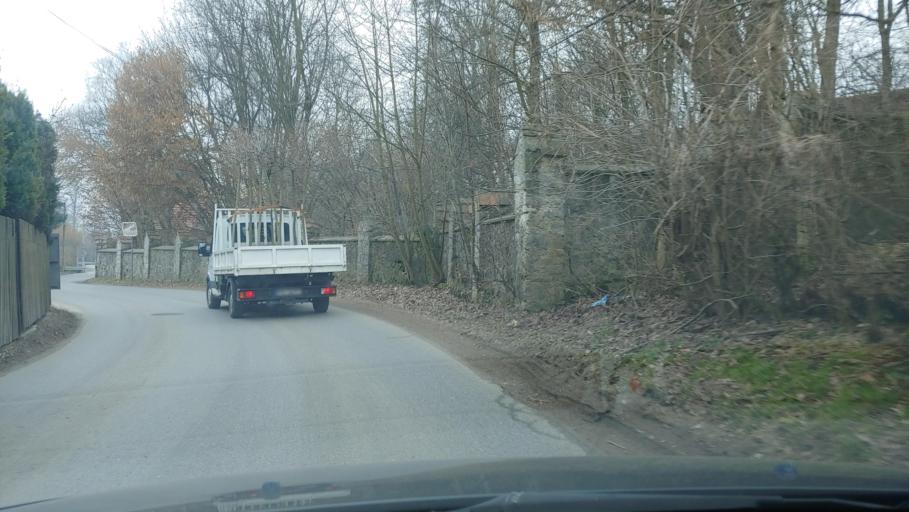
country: PL
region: Lesser Poland Voivodeship
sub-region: Powiat krakowski
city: Balice
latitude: 50.0885
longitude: 19.7888
